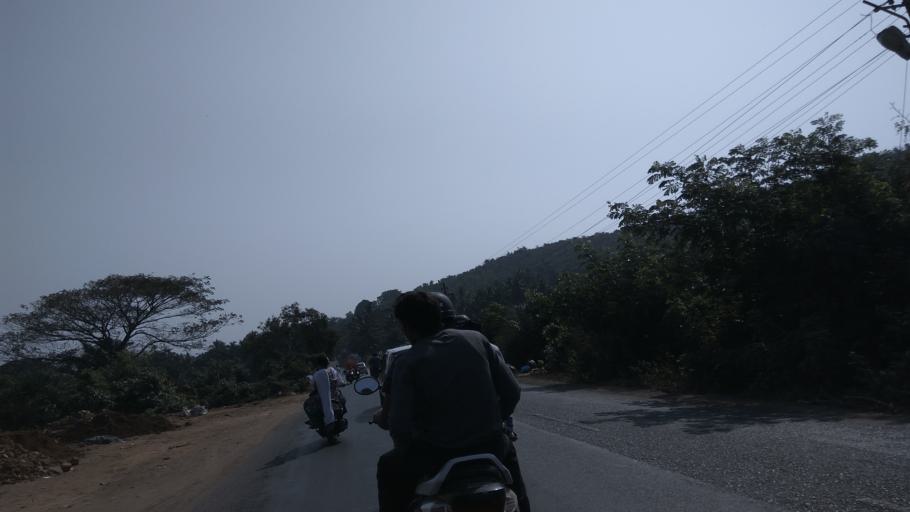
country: IN
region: Goa
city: Calangute
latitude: 15.5416
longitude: 73.7721
